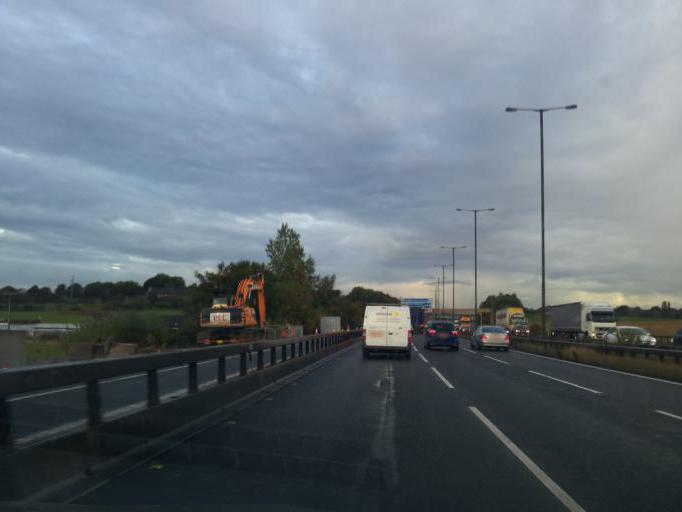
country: GB
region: England
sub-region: Manchester
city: Heywood
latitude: 53.5620
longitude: -2.2422
